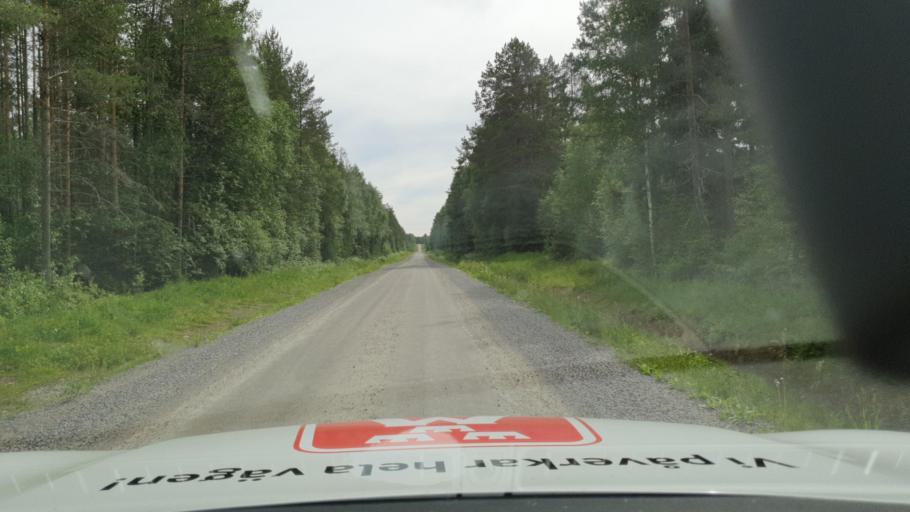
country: SE
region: Vaesterbotten
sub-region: Skelleftea Kommun
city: Burea
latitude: 64.4551
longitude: 21.0291
